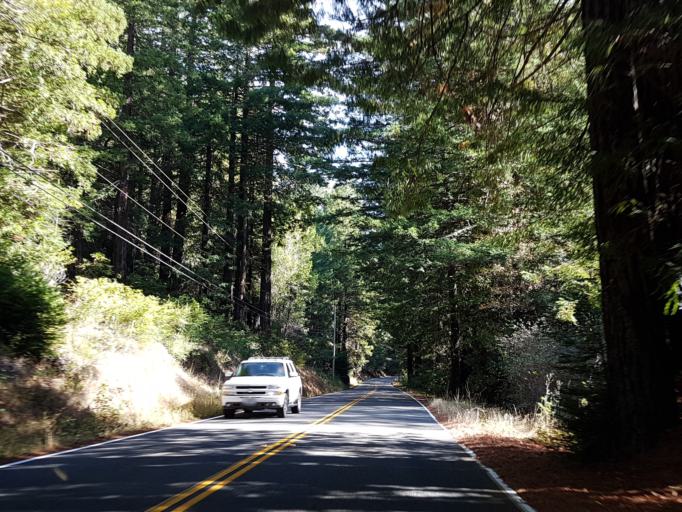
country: US
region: California
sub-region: Humboldt County
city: Rio Dell
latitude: 40.4108
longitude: -123.9572
